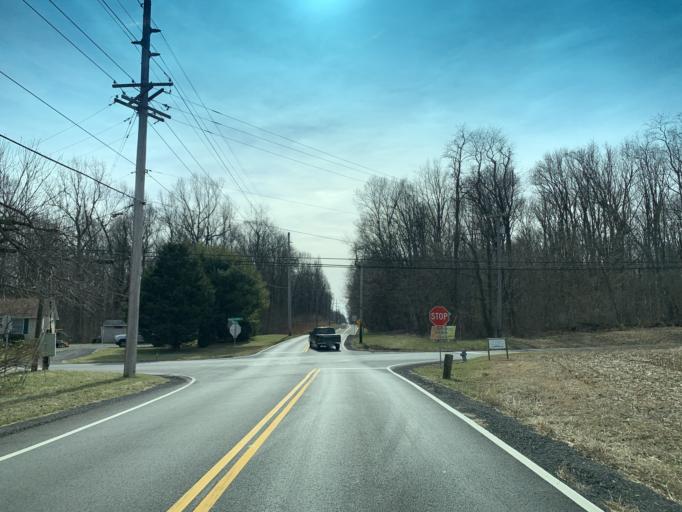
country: US
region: Maryland
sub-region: Frederick County
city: Buckeystown
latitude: 39.3314
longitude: -77.4548
